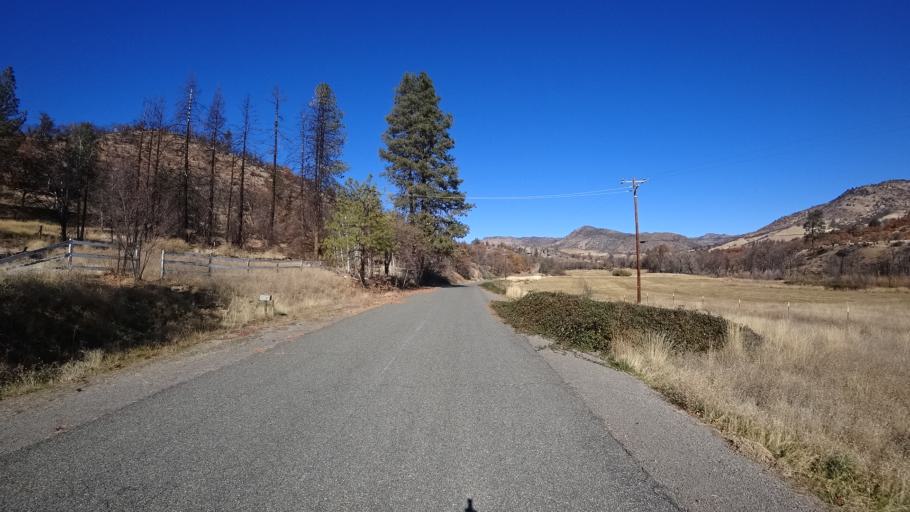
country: US
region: California
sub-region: Siskiyou County
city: Yreka
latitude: 41.9367
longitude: -122.5912
